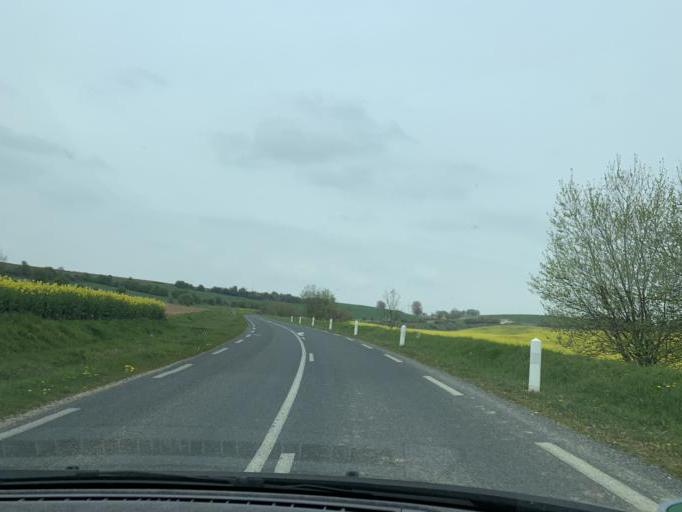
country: FR
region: Haute-Normandie
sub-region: Departement de la Seine-Maritime
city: Londinieres
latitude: 49.8396
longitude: 1.4545
